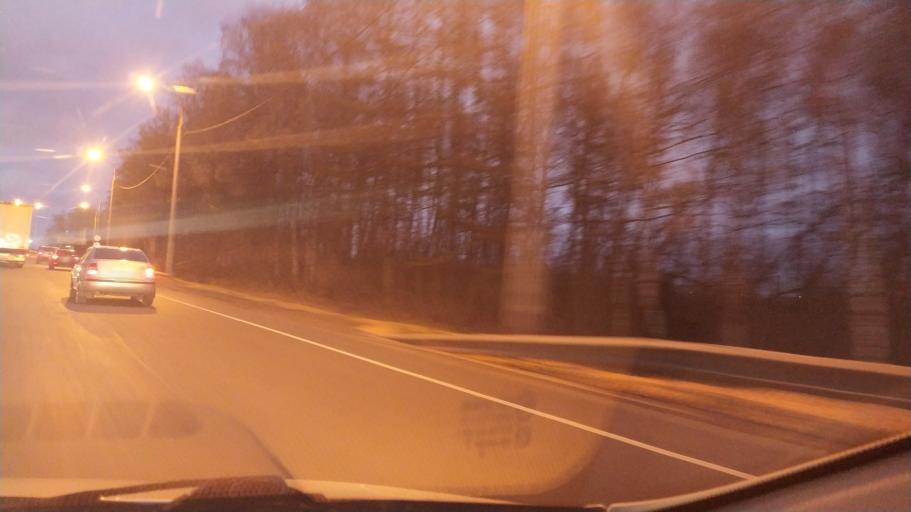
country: RU
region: Chuvashia
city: Kugesi
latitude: 56.0451
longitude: 47.2909
